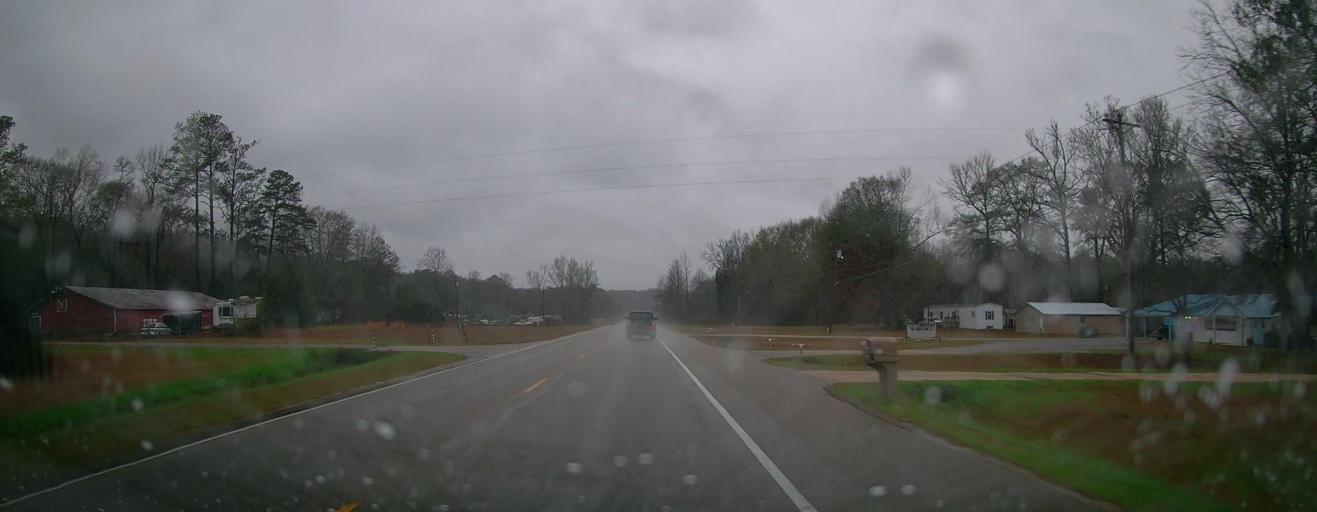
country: US
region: Alabama
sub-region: Autauga County
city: Prattville
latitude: 32.4707
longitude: -86.5097
